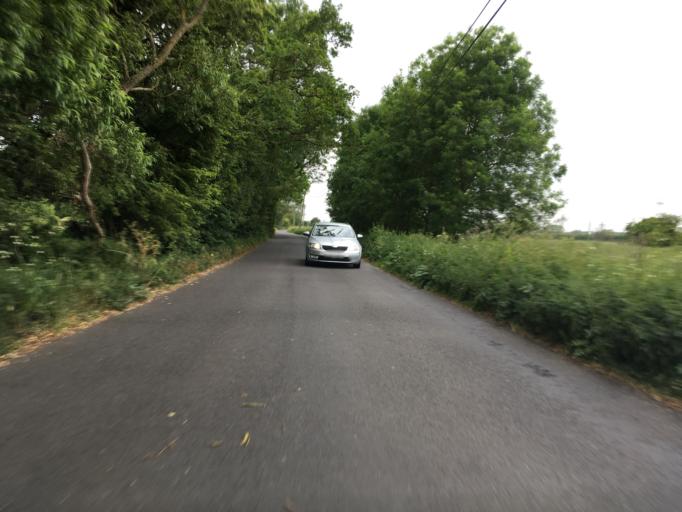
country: GB
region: England
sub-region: North Somerset
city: Kenn
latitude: 51.4237
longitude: -2.8202
